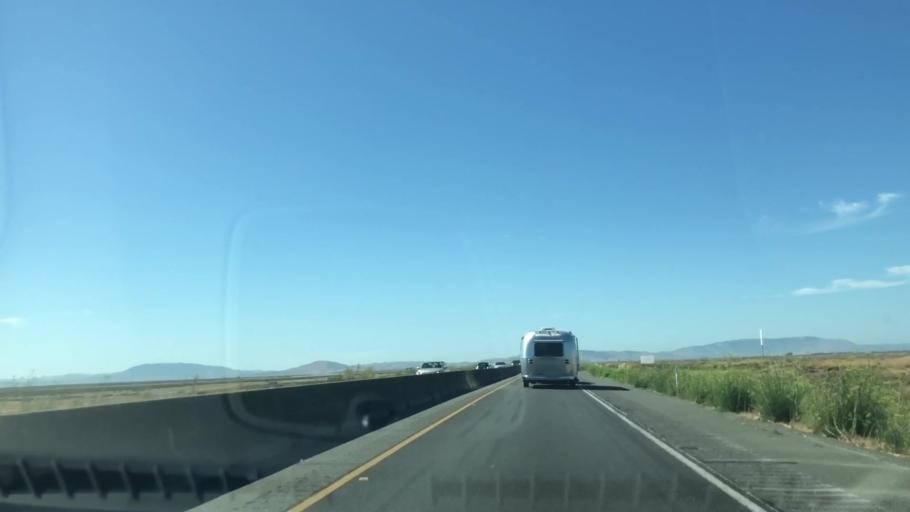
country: US
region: California
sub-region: Solano County
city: Vallejo
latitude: 38.1195
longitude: -122.3078
